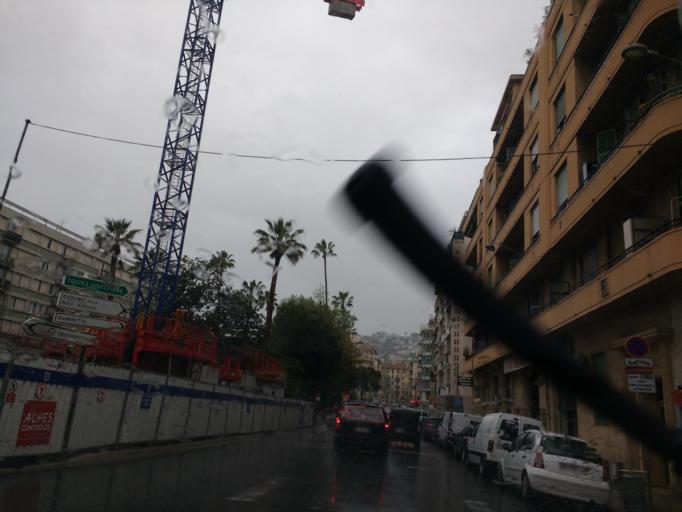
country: FR
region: Provence-Alpes-Cote d'Azur
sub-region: Departement des Alpes-Maritimes
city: Nice
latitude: 43.7062
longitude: 7.2597
